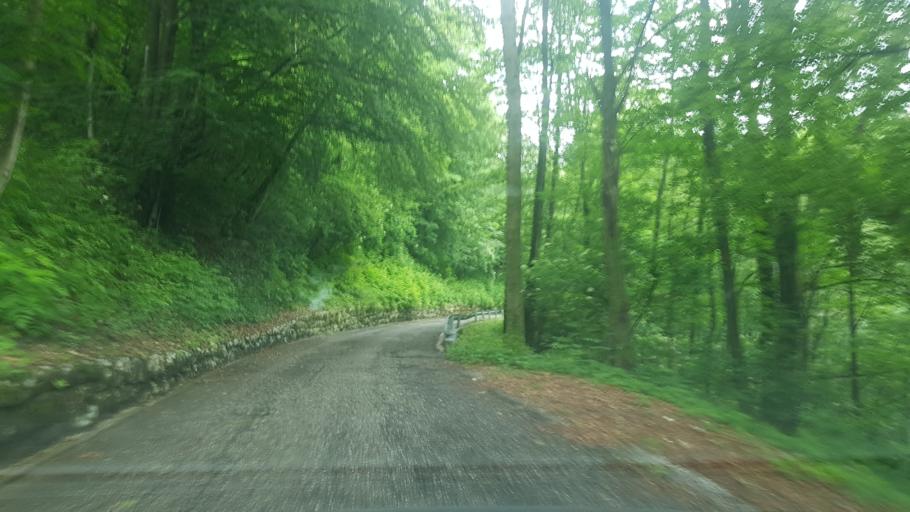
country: IT
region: Friuli Venezia Giulia
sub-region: Provincia di Udine
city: Pulfero
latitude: 46.1904
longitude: 13.4426
